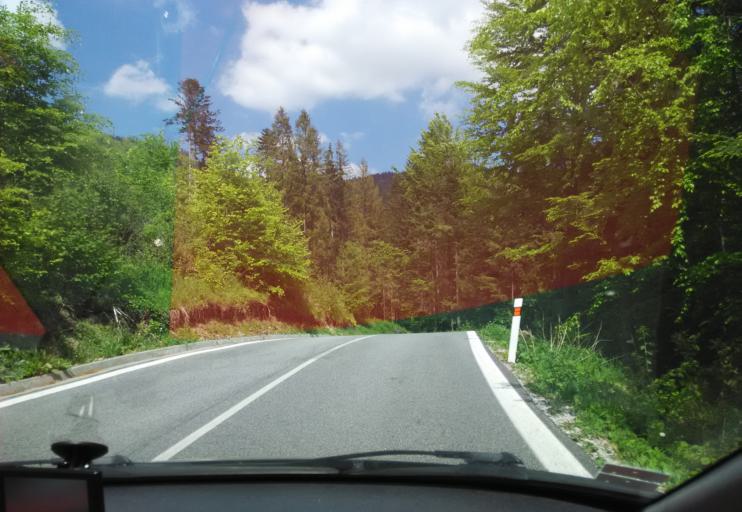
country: SK
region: Kosicky
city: Dobsina
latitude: 48.8522
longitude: 20.4549
